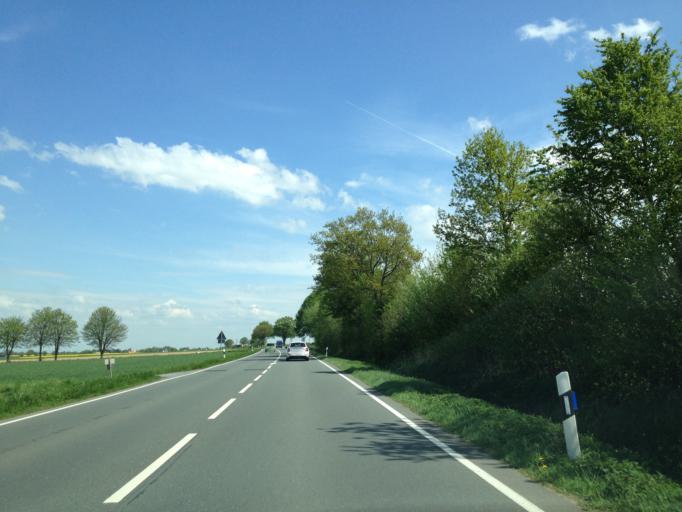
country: DE
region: North Rhine-Westphalia
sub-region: Regierungsbezirk Arnsberg
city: Mohnesee
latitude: 51.5040
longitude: 8.0400
